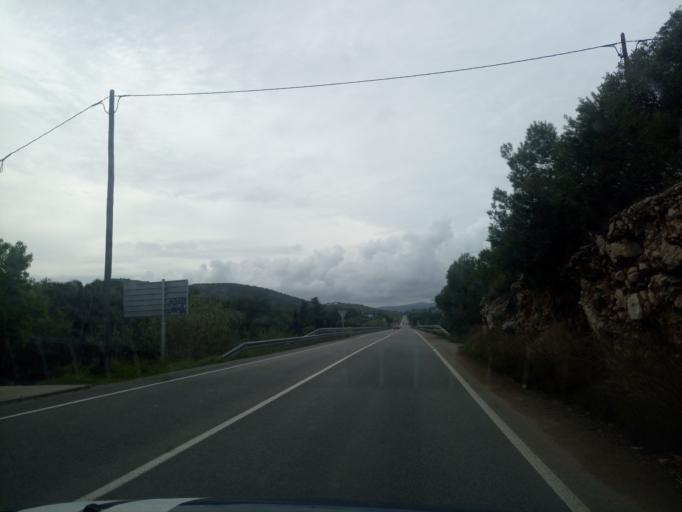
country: ES
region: Catalonia
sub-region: Provincia de Barcelona
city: Sitges
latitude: 41.2326
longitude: 1.7846
